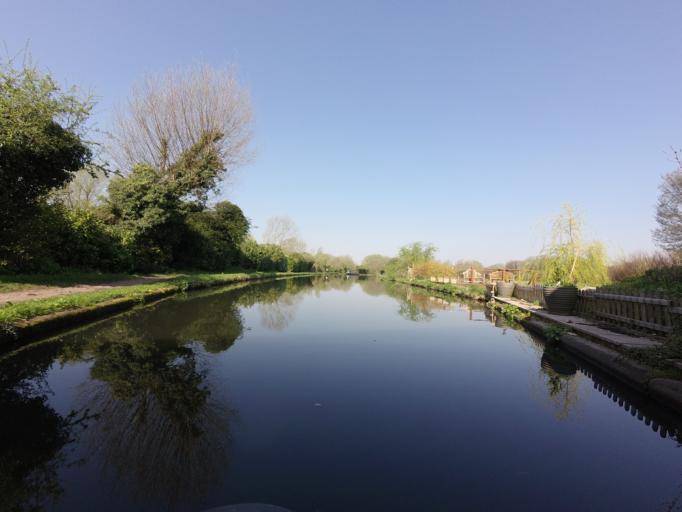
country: GB
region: England
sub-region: Hertfordshire
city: Bovingdon
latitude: 51.7477
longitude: -0.5252
